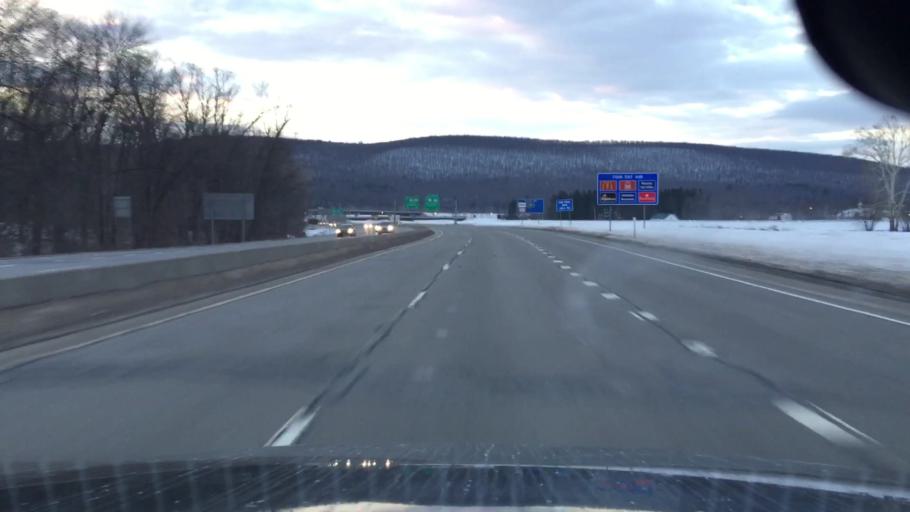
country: US
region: New York
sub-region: Steuben County
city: Painted Post
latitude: 42.1641
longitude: -77.1028
